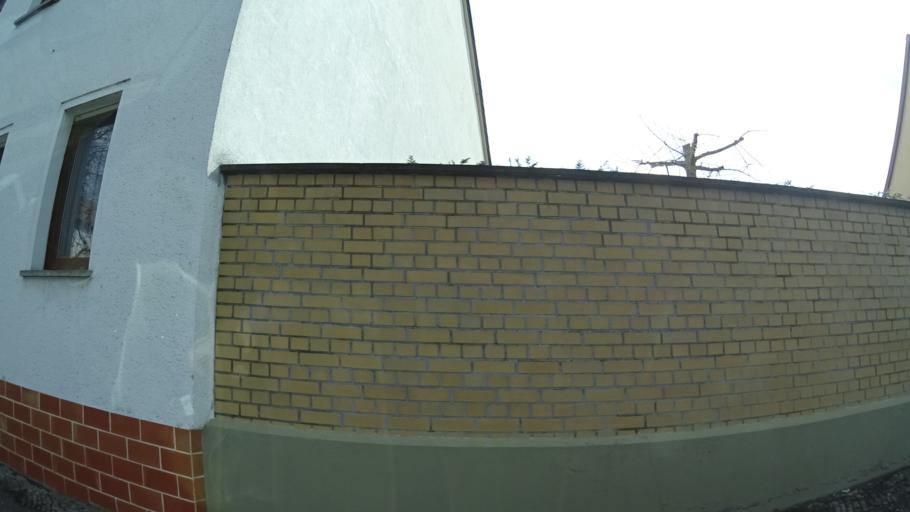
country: DE
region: Saxony-Anhalt
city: Naumburg
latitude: 51.1541
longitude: 11.8295
